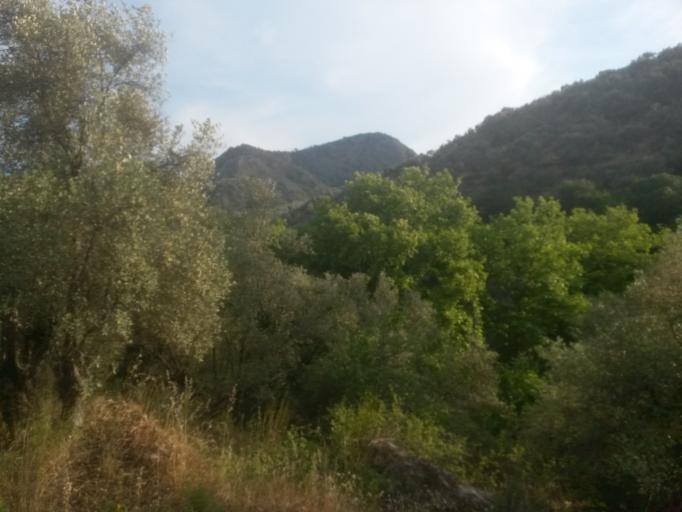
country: GR
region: North Aegean
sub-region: Nomos Lesvou
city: Agiasos
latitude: 39.1039
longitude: 26.3976
